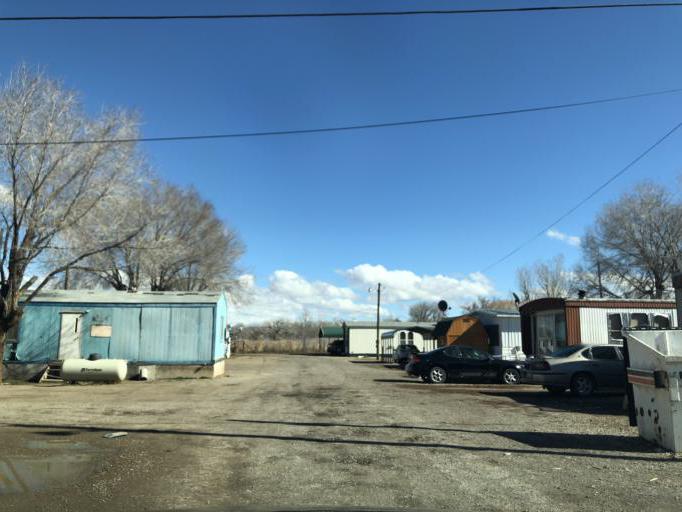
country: US
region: Utah
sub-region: Carbon County
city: East Carbon City
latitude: 38.9893
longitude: -110.1572
